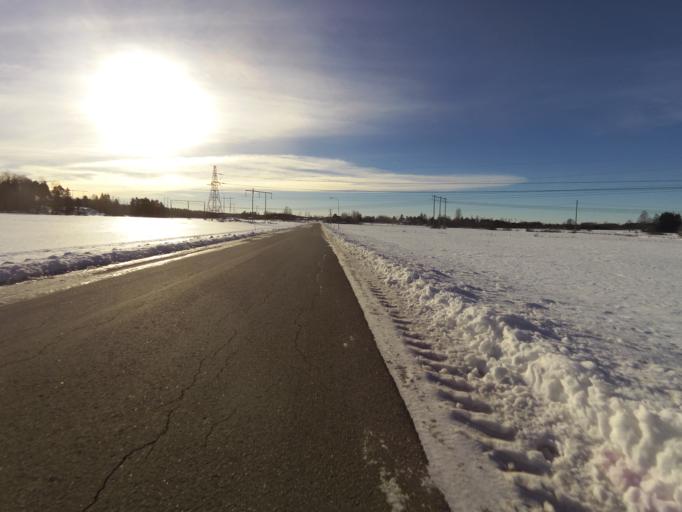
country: SE
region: Gaevleborg
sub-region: Gavle Kommun
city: Valbo
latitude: 60.6597
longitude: 17.0722
